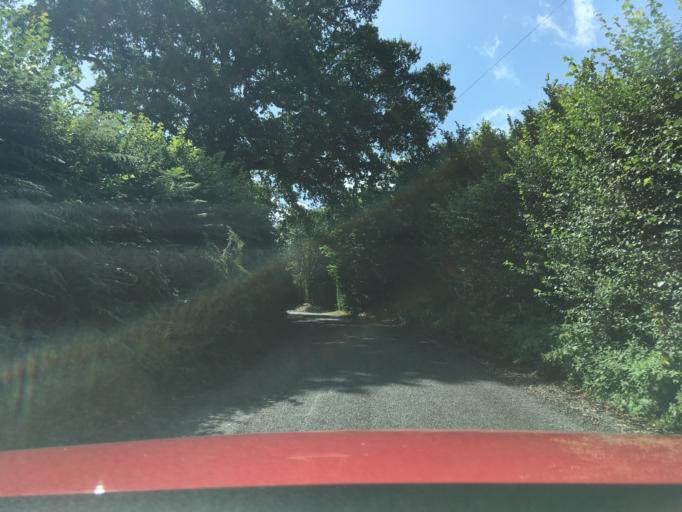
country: GB
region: England
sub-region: West Berkshire
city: Wickham
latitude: 51.4243
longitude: -1.4128
